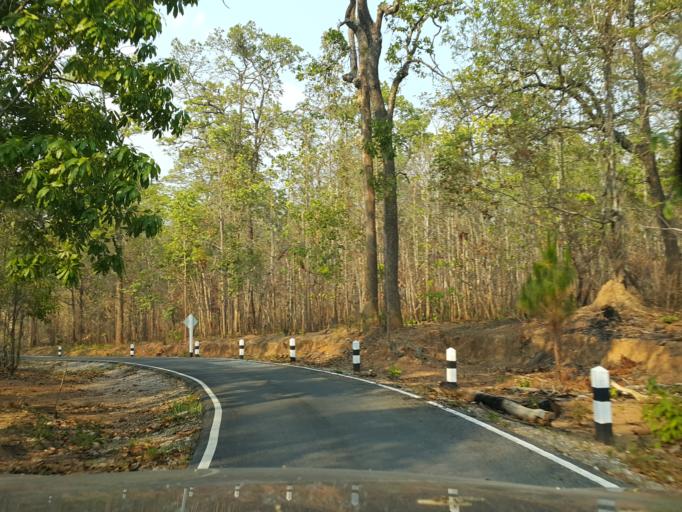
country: TH
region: Lamphun
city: Li
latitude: 17.6297
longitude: 98.8737
